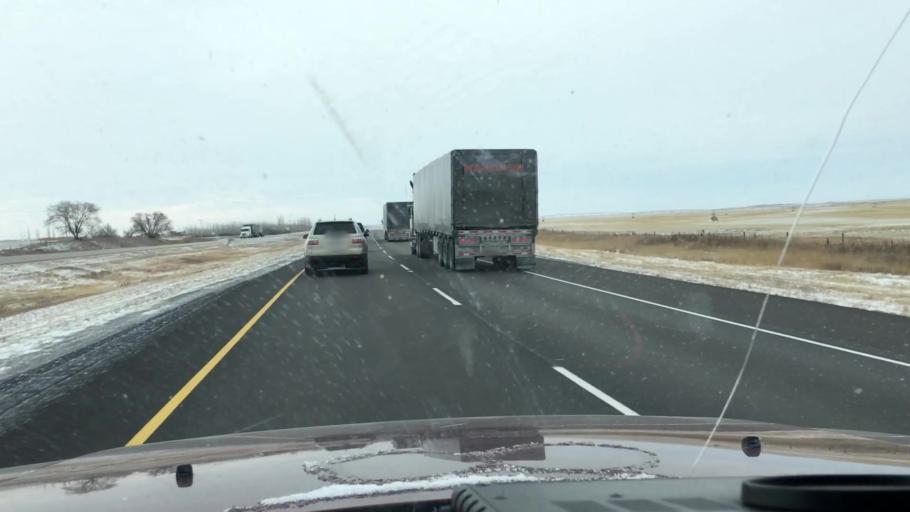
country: CA
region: Saskatchewan
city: Saskatoon
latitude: 51.7780
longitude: -106.4765
